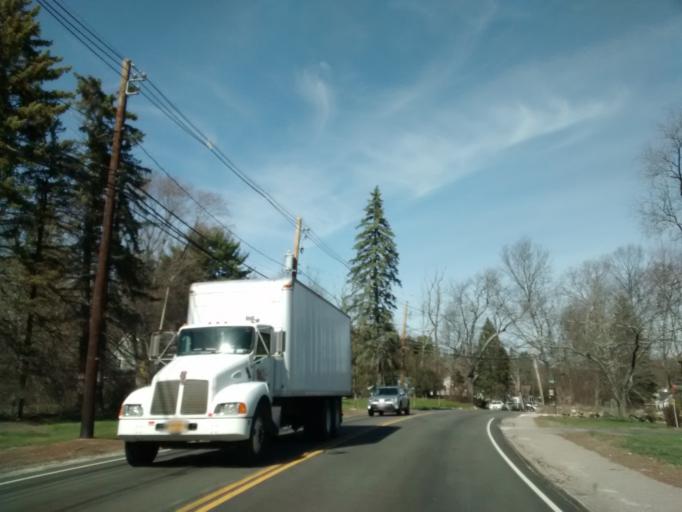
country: US
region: Massachusetts
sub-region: Norfolk County
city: Bellingham
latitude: 42.1291
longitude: -71.4517
